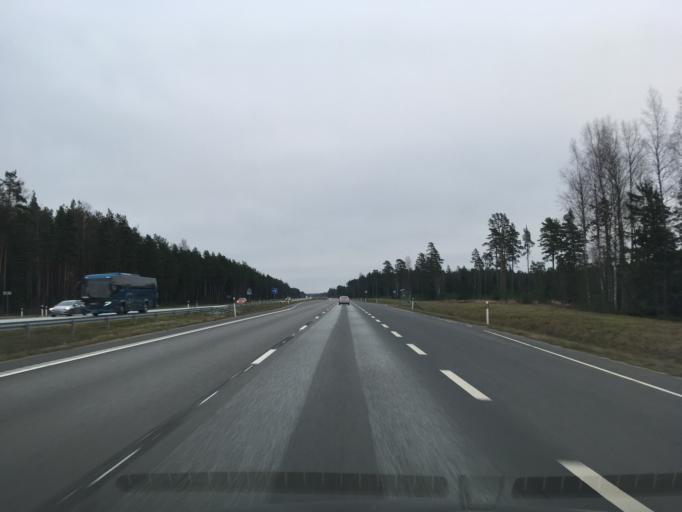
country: EE
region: Harju
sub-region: Loksa linn
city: Loksa
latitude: 59.4567
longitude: 25.8633
